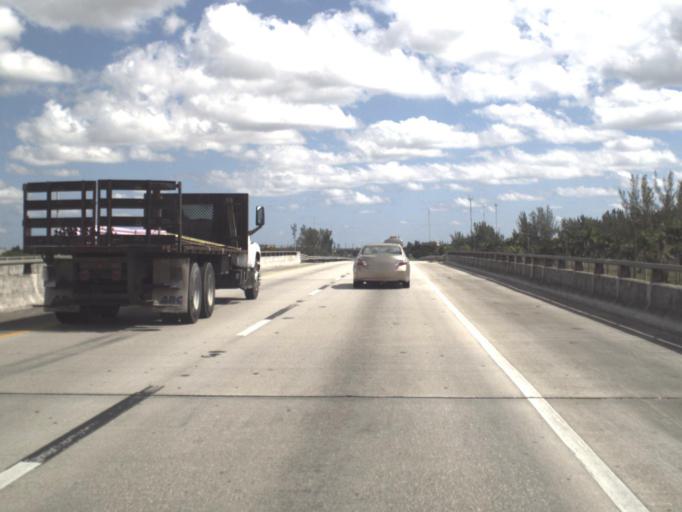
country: US
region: Florida
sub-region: Miami-Dade County
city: Lake Lucerne
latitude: 25.9713
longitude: -80.2790
